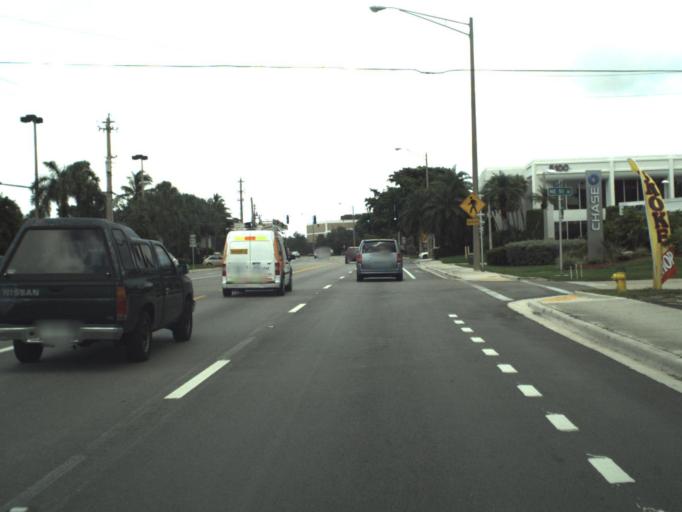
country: US
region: Florida
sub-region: Broward County
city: North Andrews Gardens
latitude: 26.1903
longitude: -80.1330
